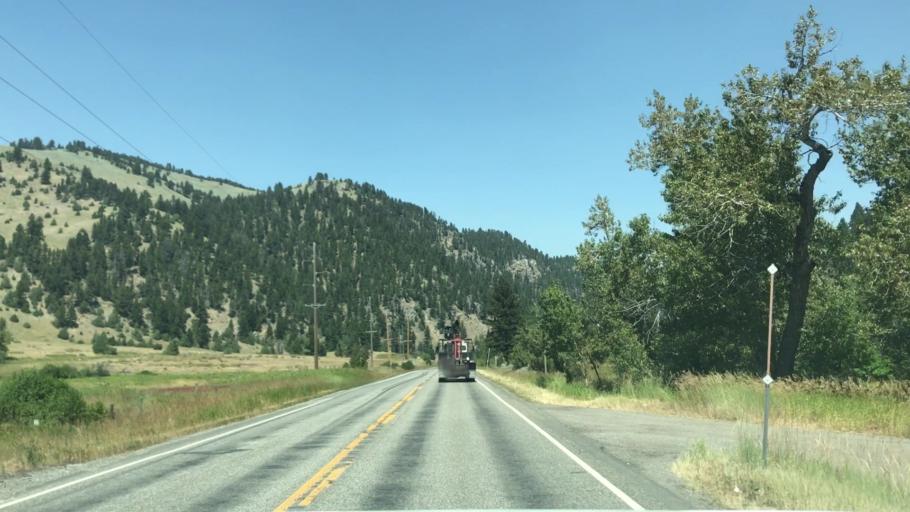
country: US
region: Montana
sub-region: Gallatin County
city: Four Corners
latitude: 45.4947
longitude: -111.2719
